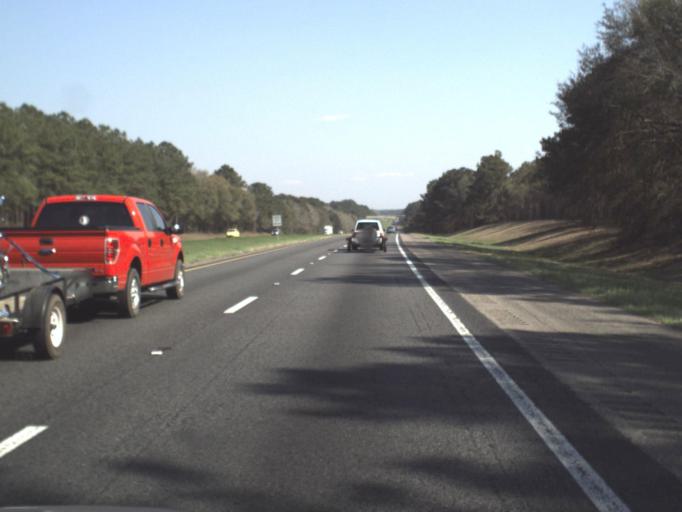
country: US
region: Florida
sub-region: Gadsden County
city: Gretna
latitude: 30.5614
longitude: -84.6449
